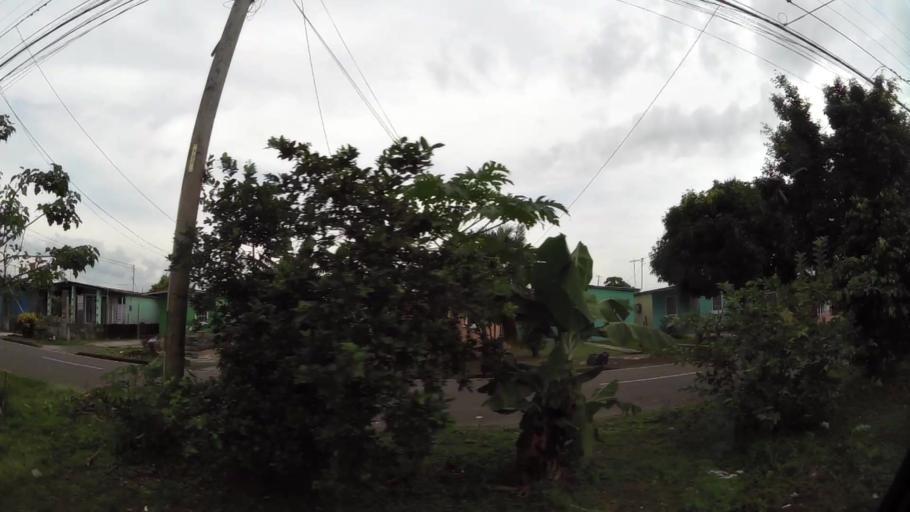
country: PA
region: Panama
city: Cabra Numero Uno
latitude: 9.0850
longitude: -79.3498
